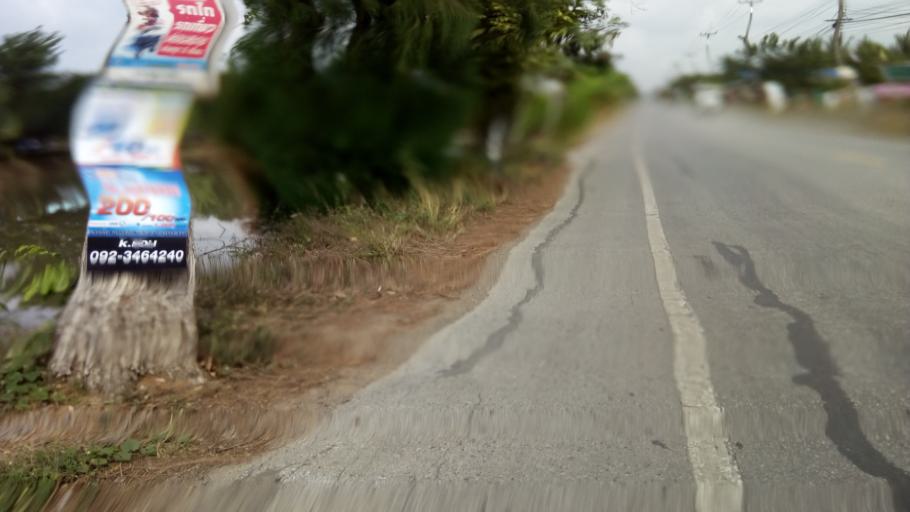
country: TH
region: Pathum Thani
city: Nong Suea
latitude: 14.1570
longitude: 100.8237
